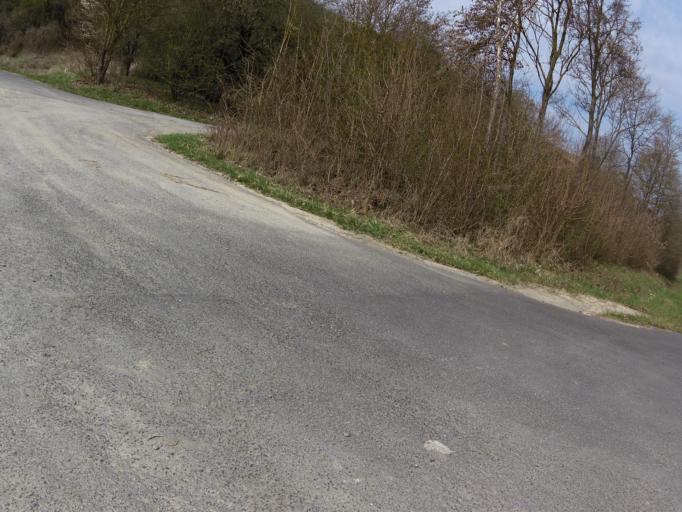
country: DE
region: Bavaria
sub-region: Regierungsbezirk Unterfranken
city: Mainstockheim
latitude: 49.7868
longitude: 10.1513
